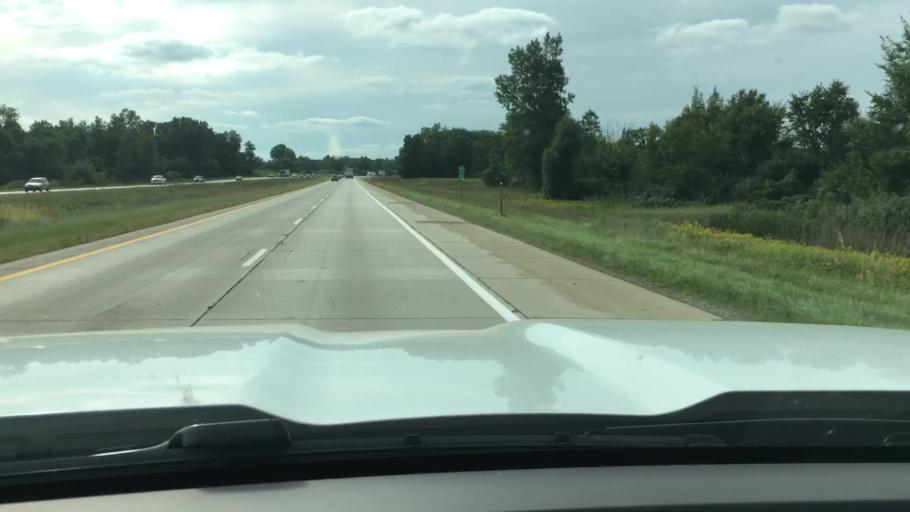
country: US
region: Michigan
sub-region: Lapeer County
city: Lapeer
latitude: 43.0119
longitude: -83.2705
